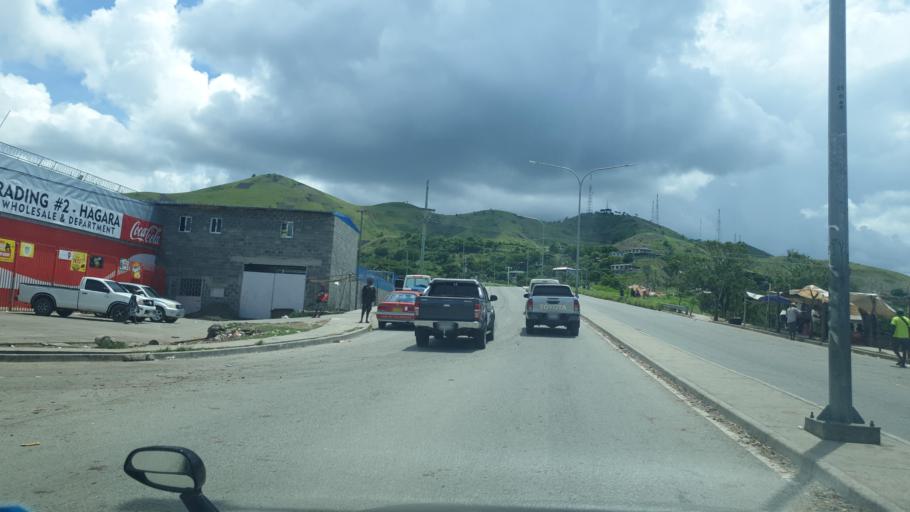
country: PG
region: National Capital
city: Port Moresby
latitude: -9.4503
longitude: 147.1511
